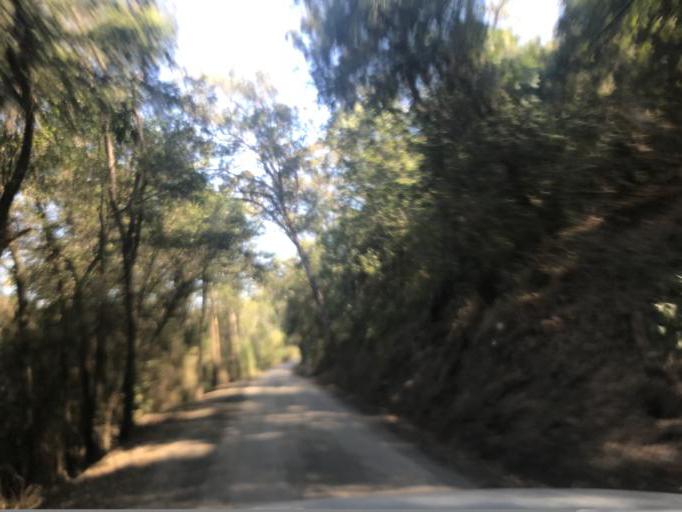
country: AU
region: New South Wales
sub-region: Hawkesbury
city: Pitt Town
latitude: -33.4188
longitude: 150.9007
